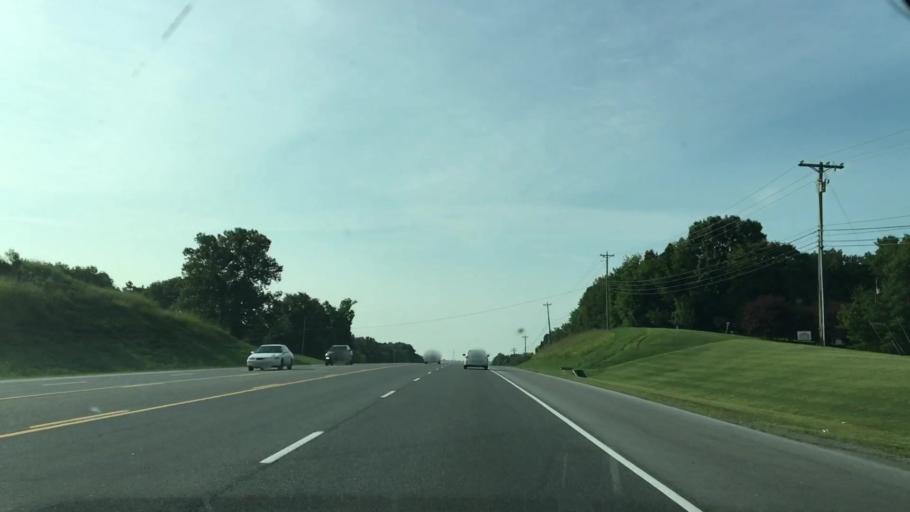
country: US
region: Tennessee
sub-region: Wilson County
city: Mount Juliet
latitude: 36.2005
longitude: -86.4156
